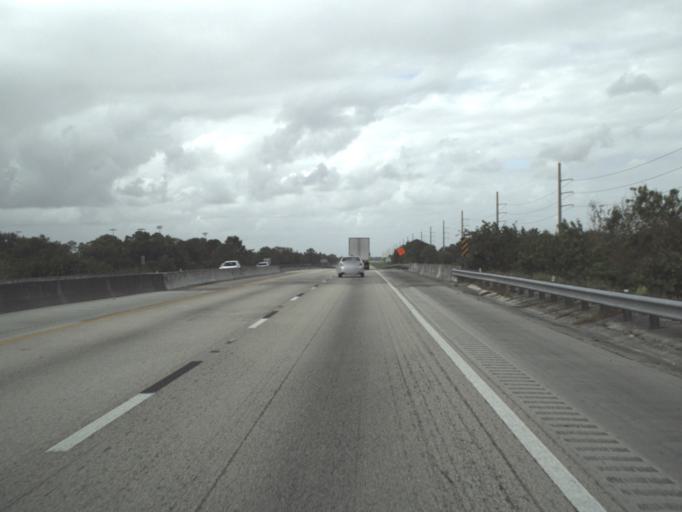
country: US
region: Florida
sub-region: Martin County
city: Palm City
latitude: 27.1737
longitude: -80.3129
